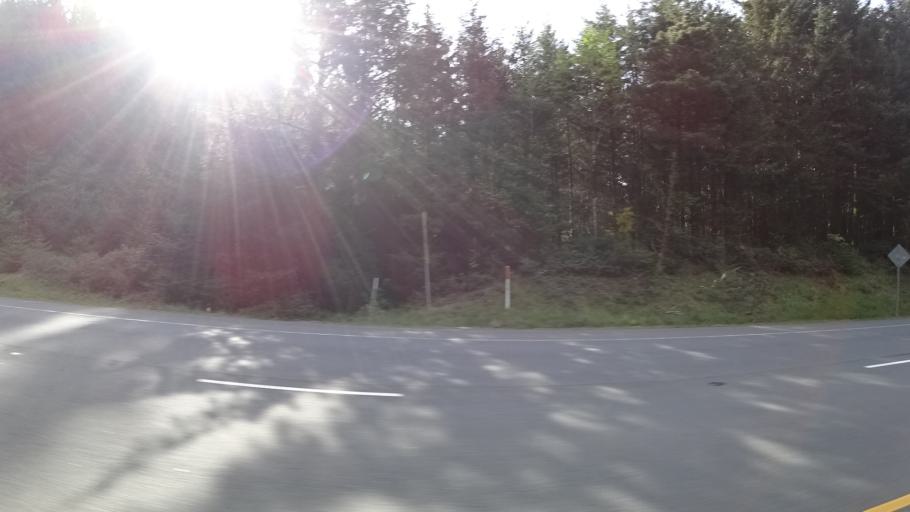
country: US
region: Oregon
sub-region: Curry County
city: Gold Beach
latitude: 42.3312
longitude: -124.4220
